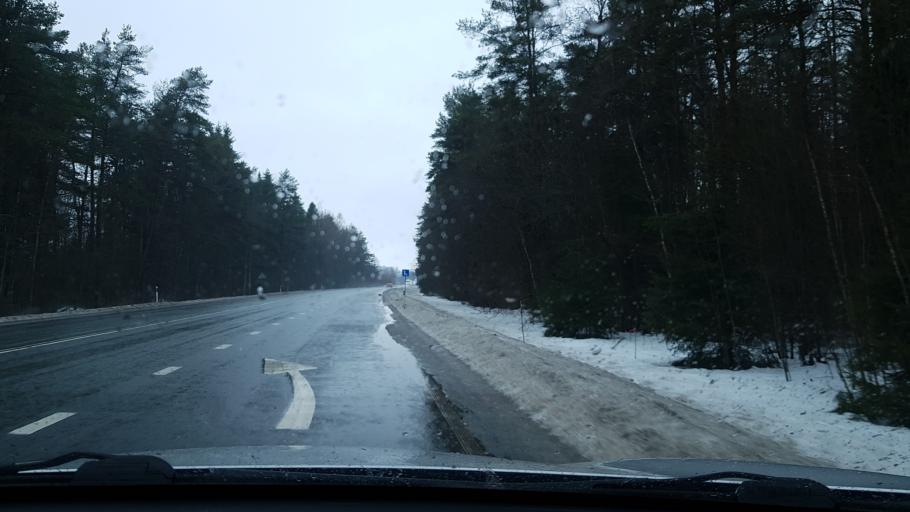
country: EE
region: Raplamaa
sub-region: Kohila vald
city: Kohila
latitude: 59.1642
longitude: 24.7719
